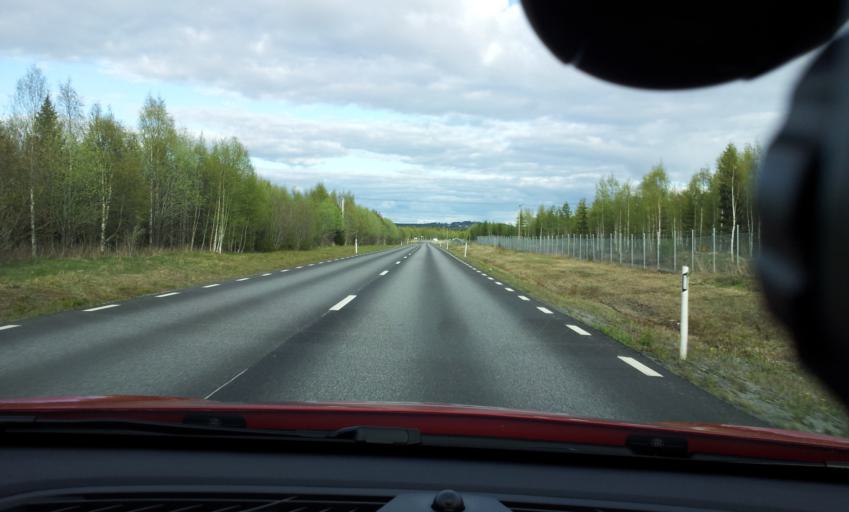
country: SE
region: Jaemtland
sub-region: Krokoms Kommun
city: Krokom
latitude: 63.2030
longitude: 14.4850
